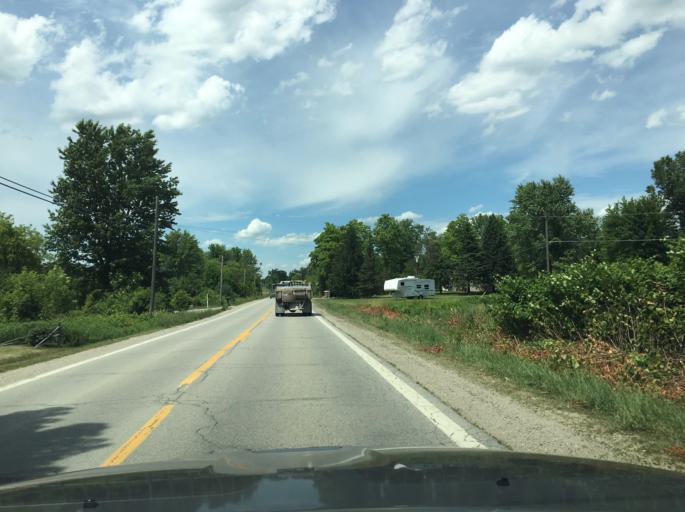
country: US
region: Michigan
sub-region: Macomb County
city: Romeo
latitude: 42.7718
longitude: -82.9614
